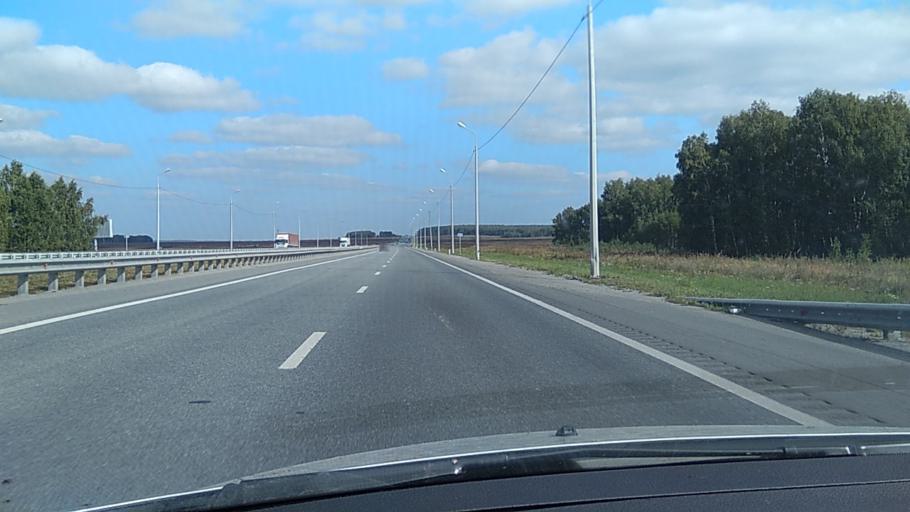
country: RU
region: Chelyabinsk
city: Chebarkul'
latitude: 54.9103
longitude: 60.4446
